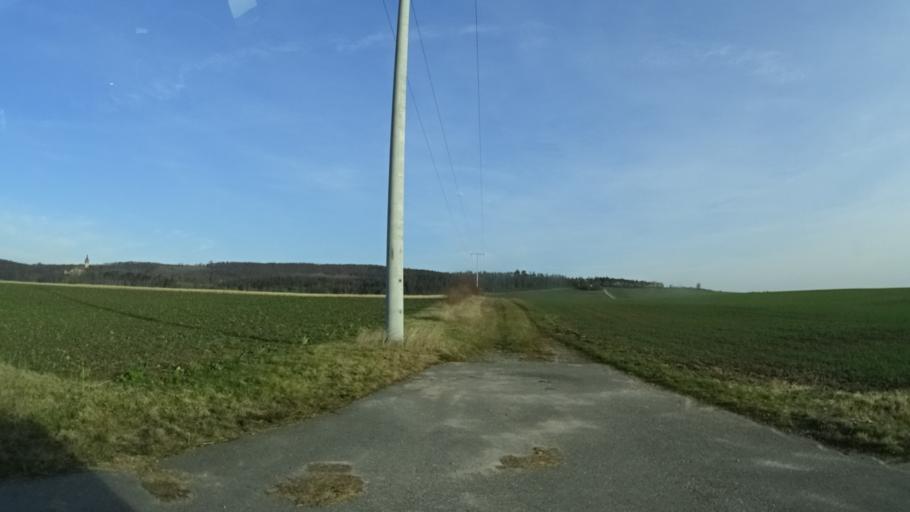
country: DE
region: Thuringia
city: Tonndorf
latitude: 50.8853
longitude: 11.2195
